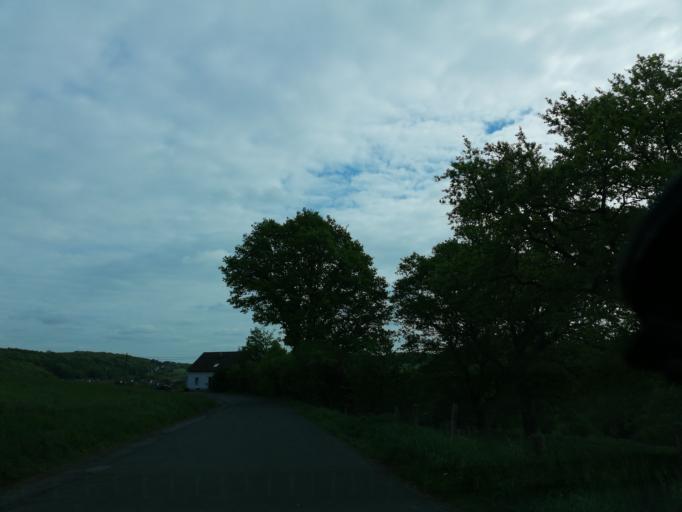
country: DE
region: North Rhine-Westphalia
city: Gevelsberg
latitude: 51.3639
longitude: 7.3054
